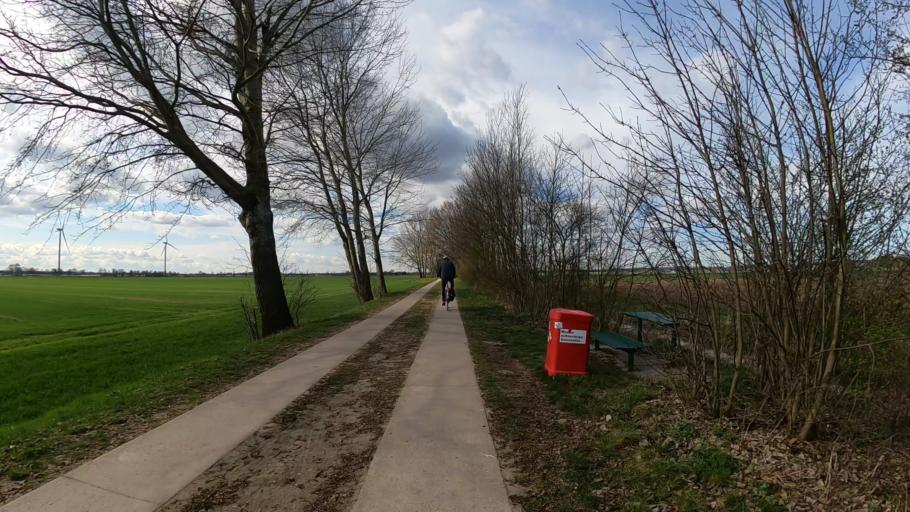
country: DE
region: Lower Saxony
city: Stelle
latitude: 53.4633
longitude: 10.1026
